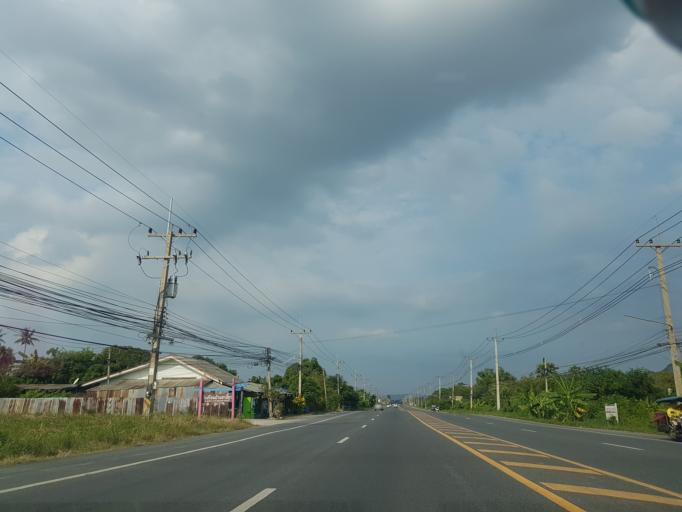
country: TH
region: Sara Buri
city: Phra Phutthabat
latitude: 14.6934
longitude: 100.7776
